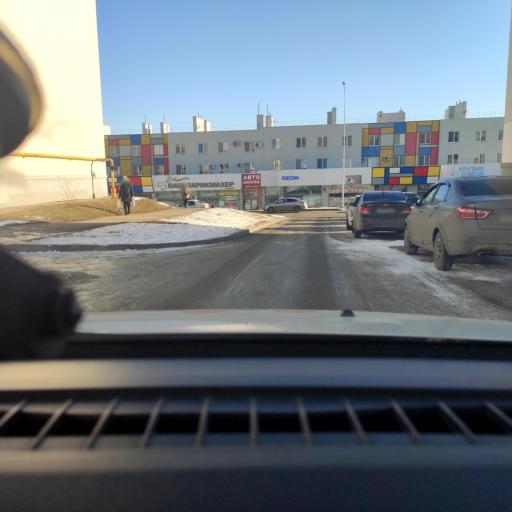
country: RU
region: Samara
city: Petra-Dubrava
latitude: 53.3242
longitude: 50.3143
